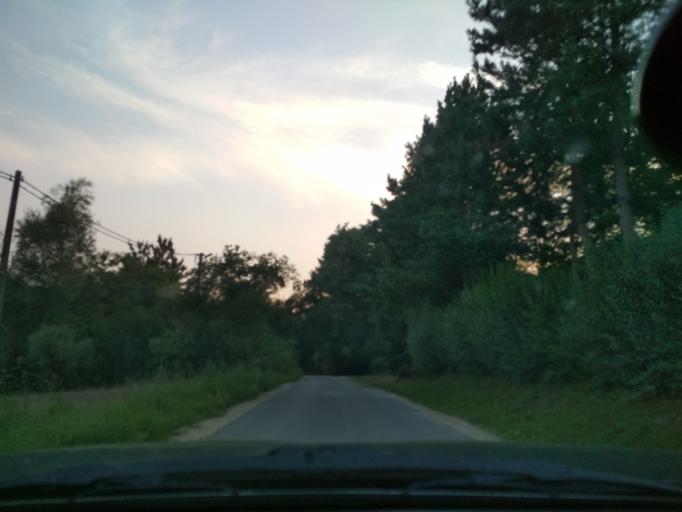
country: PL
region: Lesser Poland Voivodeship
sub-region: Powiat olkuski
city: Wolbrom
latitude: 50.4163
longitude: 19.8377
